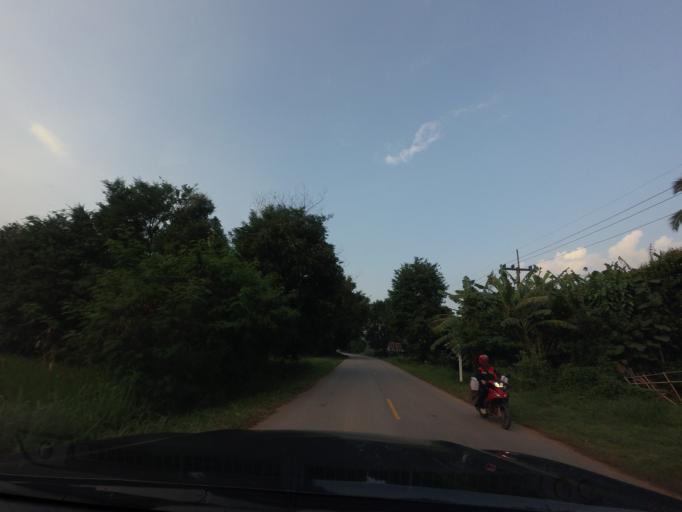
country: TH
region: Loei
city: Na Haeo
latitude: 17.4461
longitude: 101.0559
